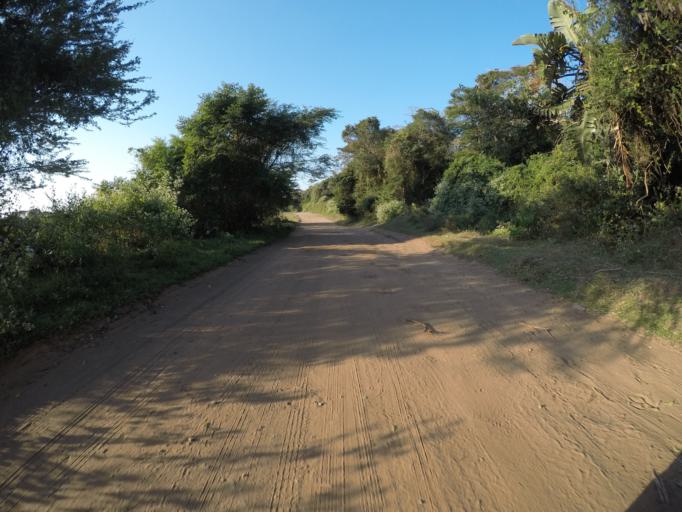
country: ZA
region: KwaZulu-Natal
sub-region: uThungulu District Municipality
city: KwaMbonambi
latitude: -28.7046
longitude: 32.1881
